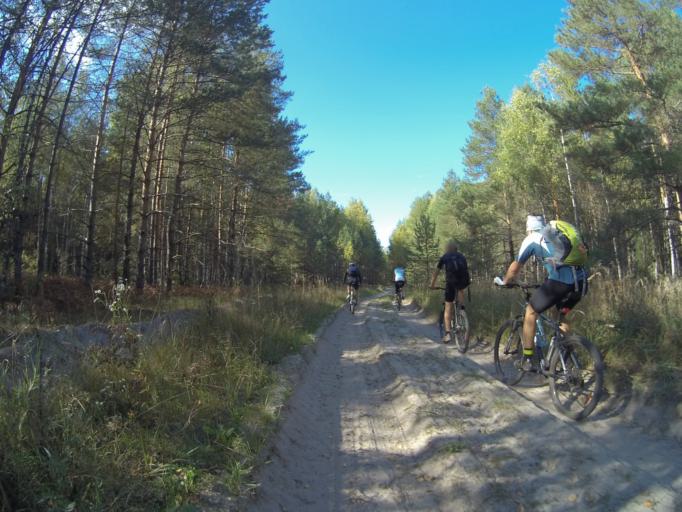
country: RU
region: Vladimir
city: Vorsha
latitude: 55.9174
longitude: 40.1515
